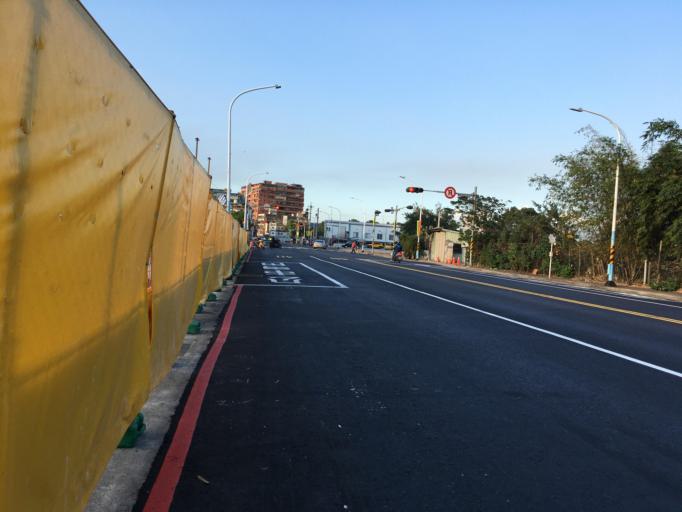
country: TW
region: Taipei
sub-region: Taipei
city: Banqiao
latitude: 25.0261
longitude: 121.4348
